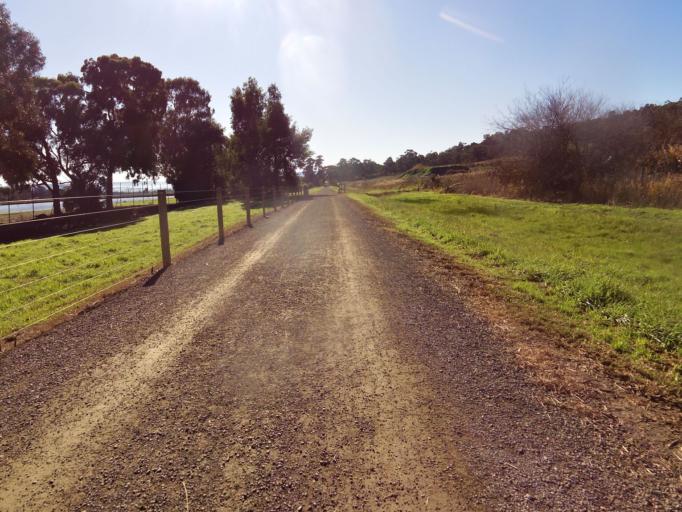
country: AU
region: Victoria
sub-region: Yarra Ranges
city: Lilydale
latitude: -37.7431
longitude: 145.3594
